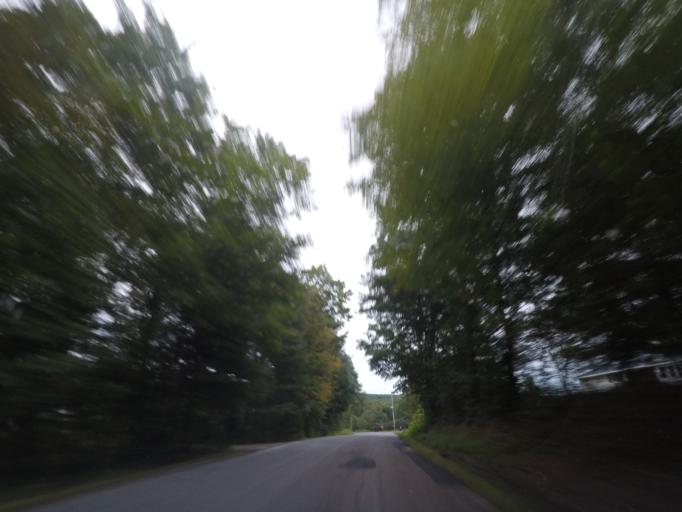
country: US
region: New York
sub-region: Rensselaer County
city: West Sand Lake
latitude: 42.5863
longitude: -73.6045
